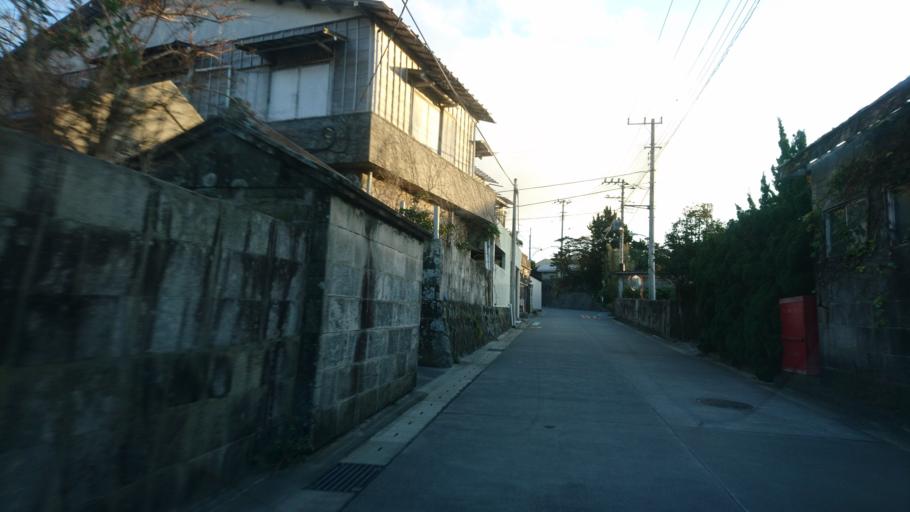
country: JP
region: Shizuoka
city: Shimoda
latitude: 34.3759
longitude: 139.2574
